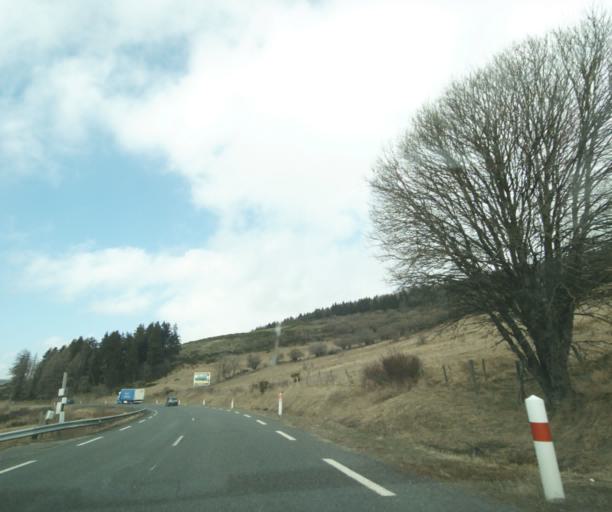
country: FR
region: Languedoc-Roussillon
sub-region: Departement de la Lozere
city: Mende
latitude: 44.6180
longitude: 3.6779
